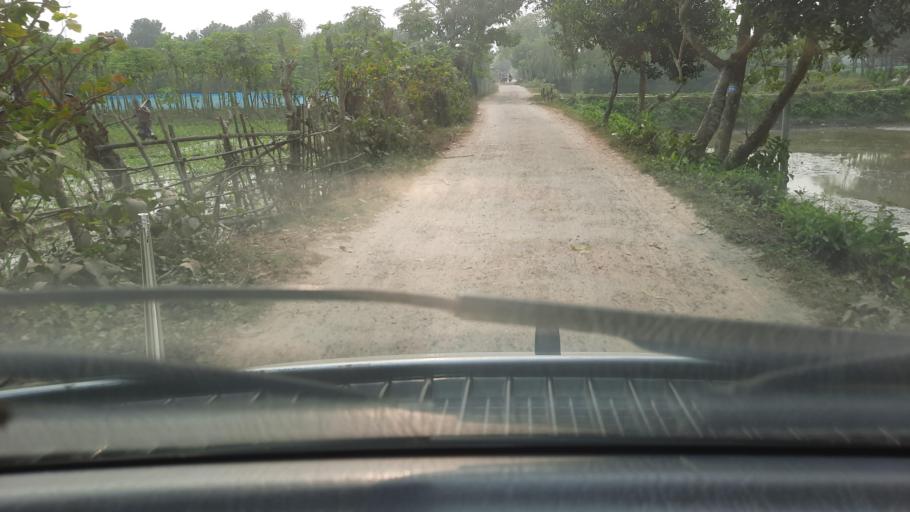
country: BD
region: Khulna
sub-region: Chuadanga
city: Nowlamary
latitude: 23.6052
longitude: 88.8595
